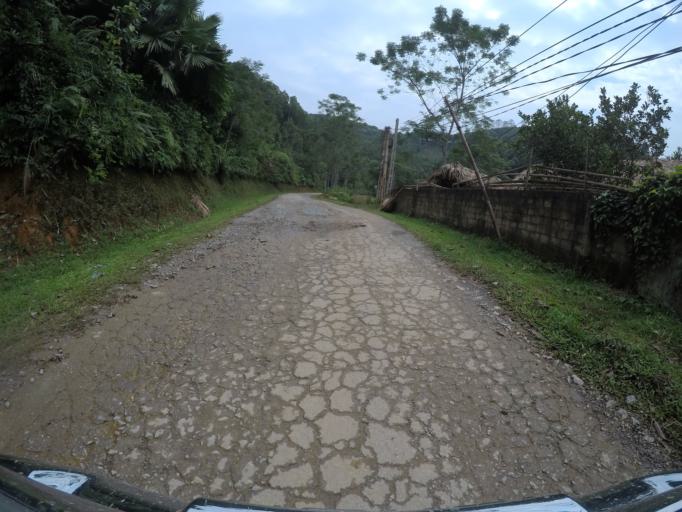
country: VN
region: Yen Bai
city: Co Phuc
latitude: 21.8214
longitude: 104.6233
